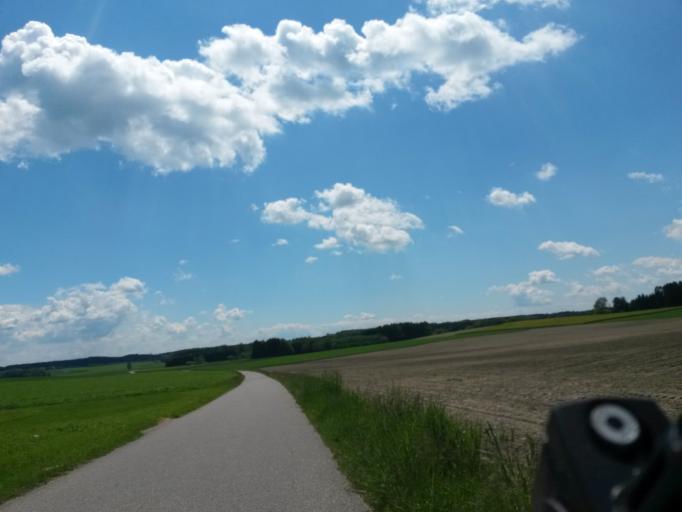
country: DE
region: Baden-Wuerttemberg
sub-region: Tuebingen Region
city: Ingoldingen
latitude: 47.9825
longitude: 9.7139
